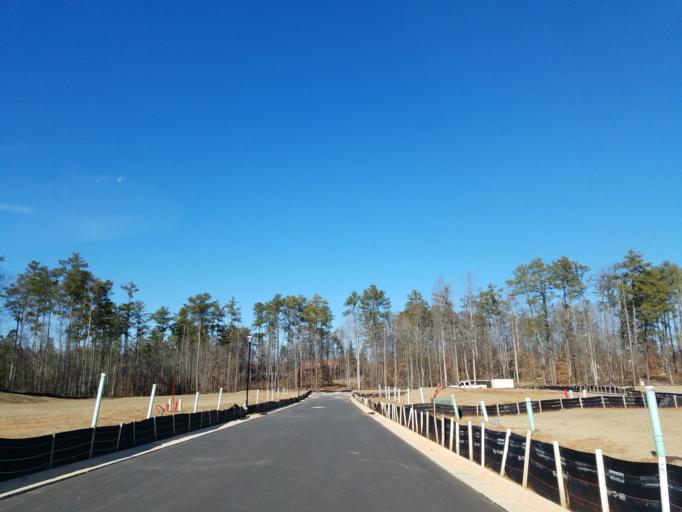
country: US
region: Georgia
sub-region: Fulton County
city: Alpharetta
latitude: 34.0509
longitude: -84.3196
